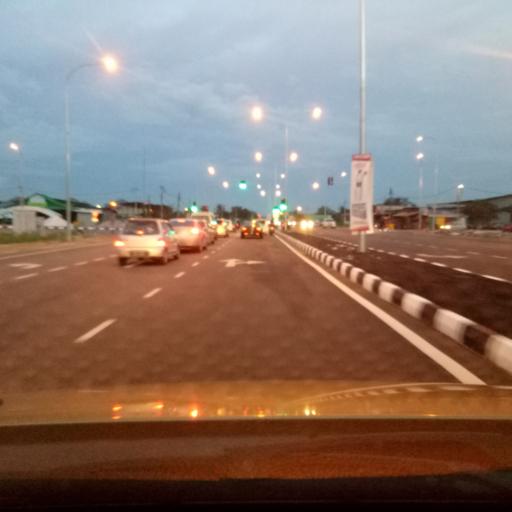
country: MY
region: Kedah
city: Alor Setar
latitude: 6.0936
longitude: 100.3833
